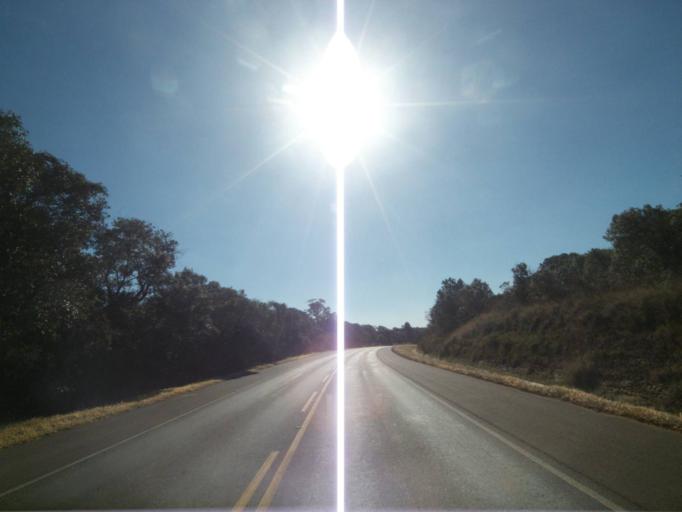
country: BR
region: Parana
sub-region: Tibagi
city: Tibagi
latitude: -24.6835
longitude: -50.4435
